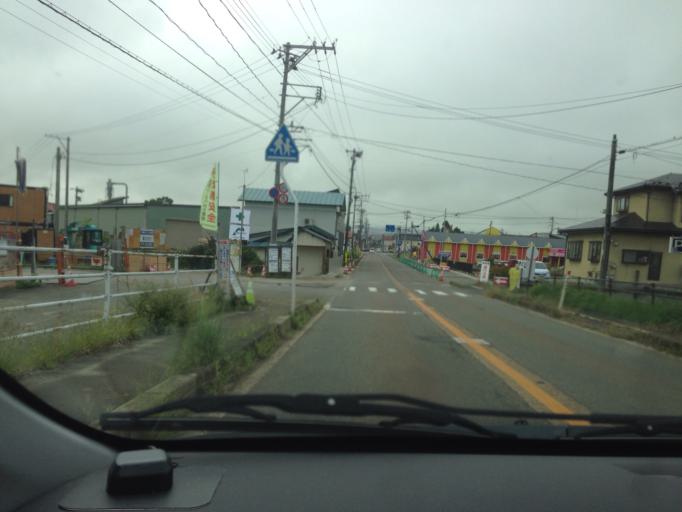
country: JP
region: Fukushima
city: Kitakata
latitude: 37.5651
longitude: 139.8267
